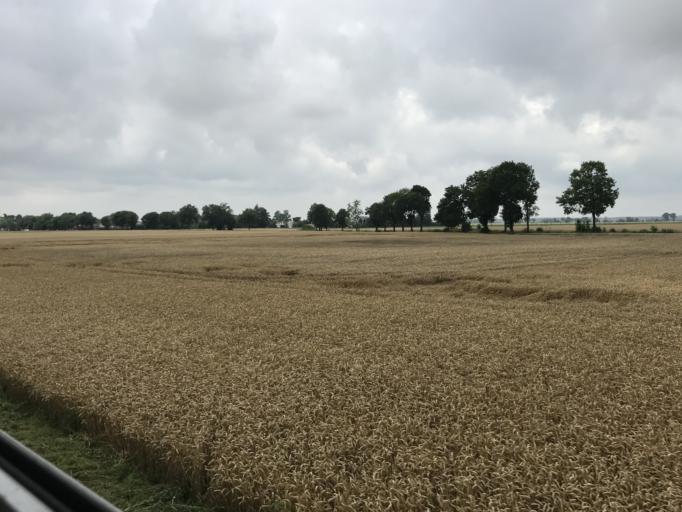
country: PL
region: Pomeranian Voivodeship
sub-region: Powiat malborski
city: Stare Pole
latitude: 54.0572
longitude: 19.2218
